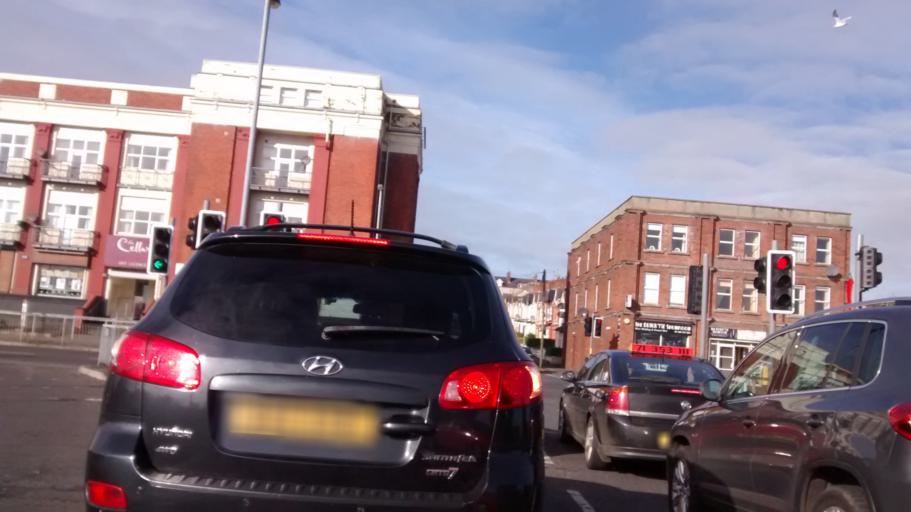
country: GB
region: Northern Ireland
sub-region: City of Derry
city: Derry
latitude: 55.0095
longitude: -7.3176
